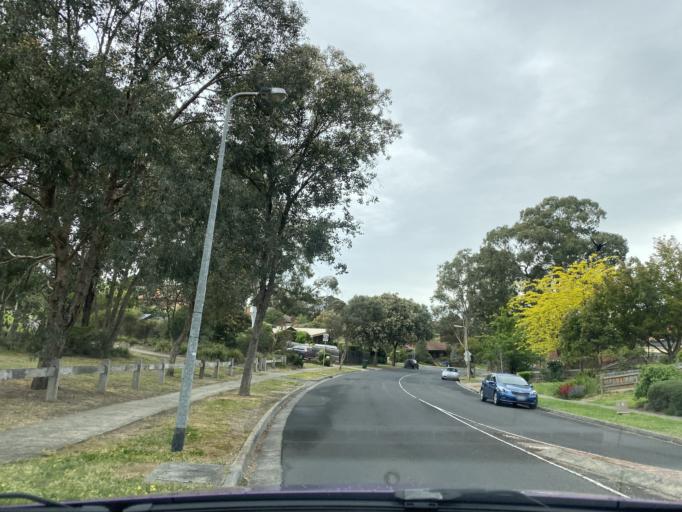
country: AU
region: Victoria
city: Saint Helena
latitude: -37.6885
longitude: 145.1363
